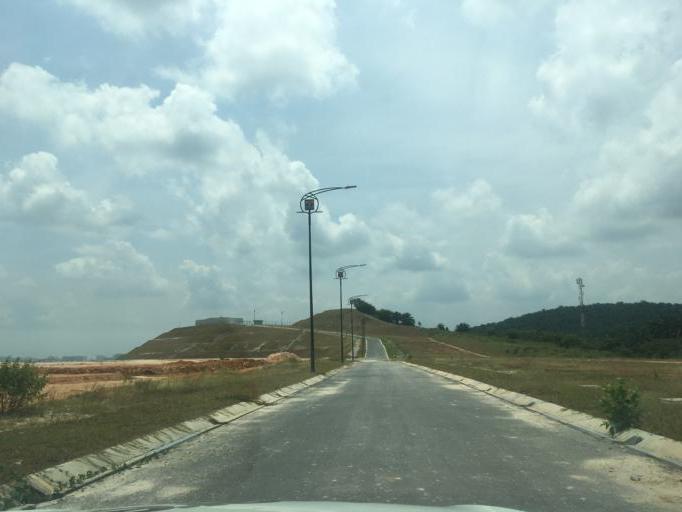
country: MY
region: Putrajaya
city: Putrajaya
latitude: 2.8451
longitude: 101.7110
